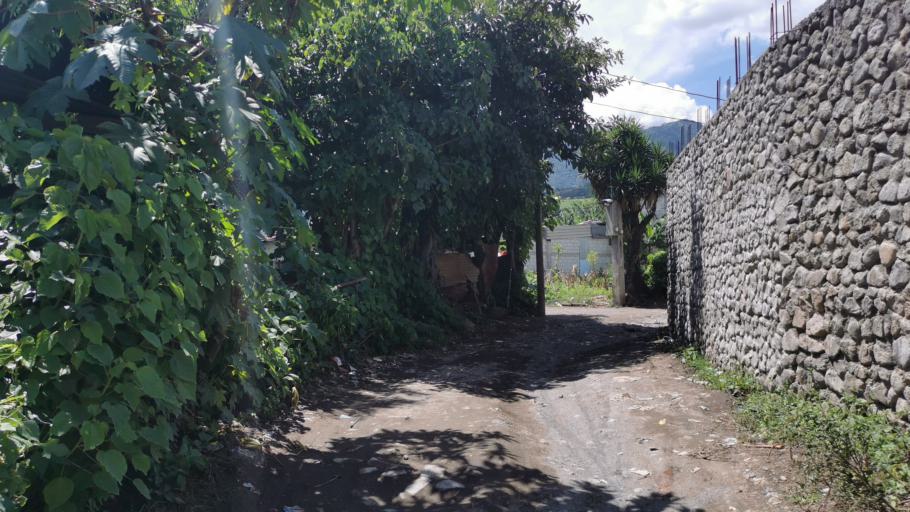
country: GT
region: Guatemala
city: Amatitlan
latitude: 14.4845
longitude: -90.6387
